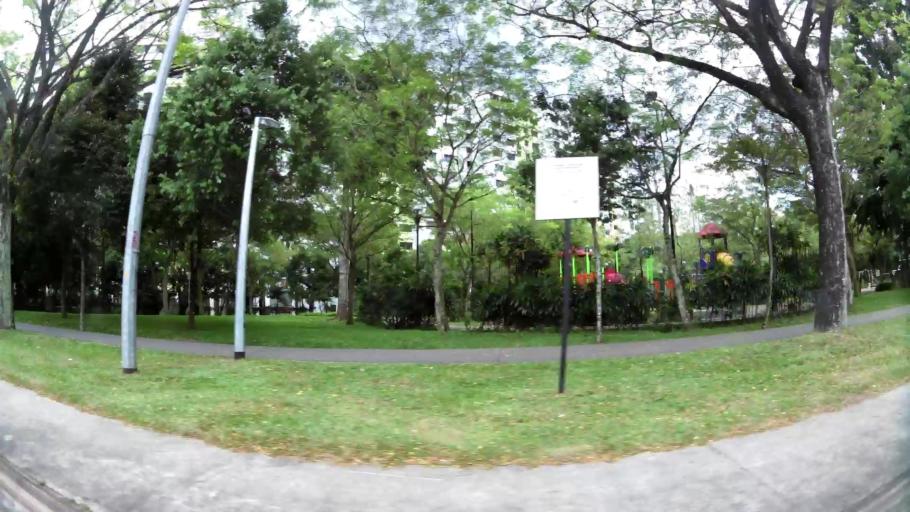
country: MY
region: Johor
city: Kampung Pasir Gudang Baru
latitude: 1.4491
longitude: 103.8253
